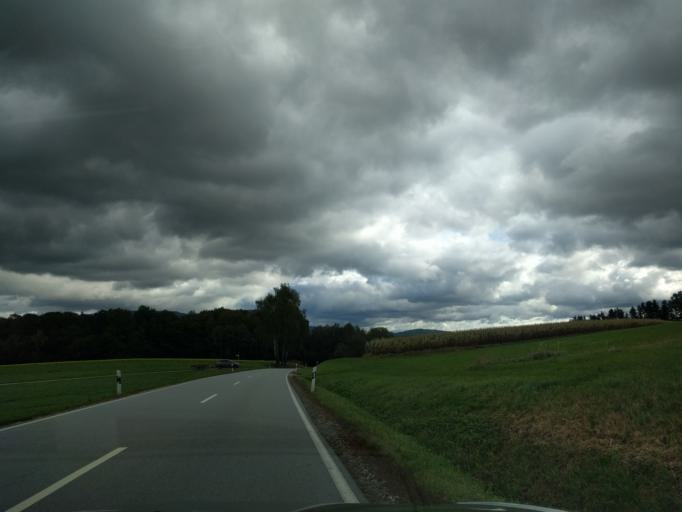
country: DE
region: Bavaria
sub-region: Lower Bavaria
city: Schaufling
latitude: 48.8365
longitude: 13.0758
